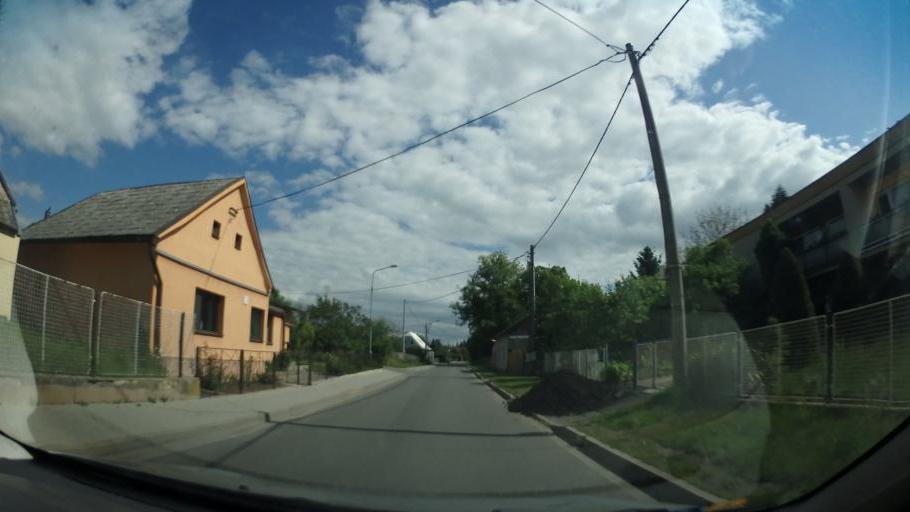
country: CZ
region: Pardubicky
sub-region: Okres Svitavy
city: Moravska Trebova
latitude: 49.7644
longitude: 16.6502
